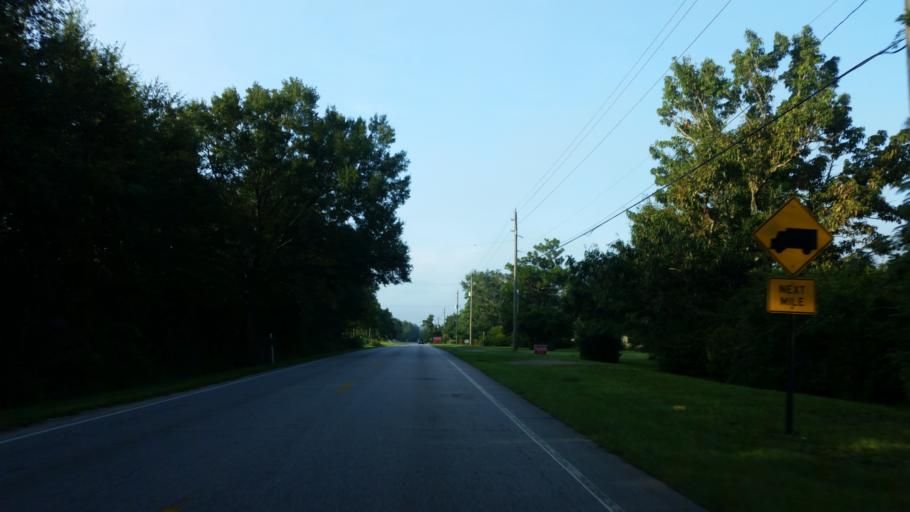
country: US
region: Florida
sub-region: Escambia County
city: Cantonment
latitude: 30.6569
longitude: -87.3221
